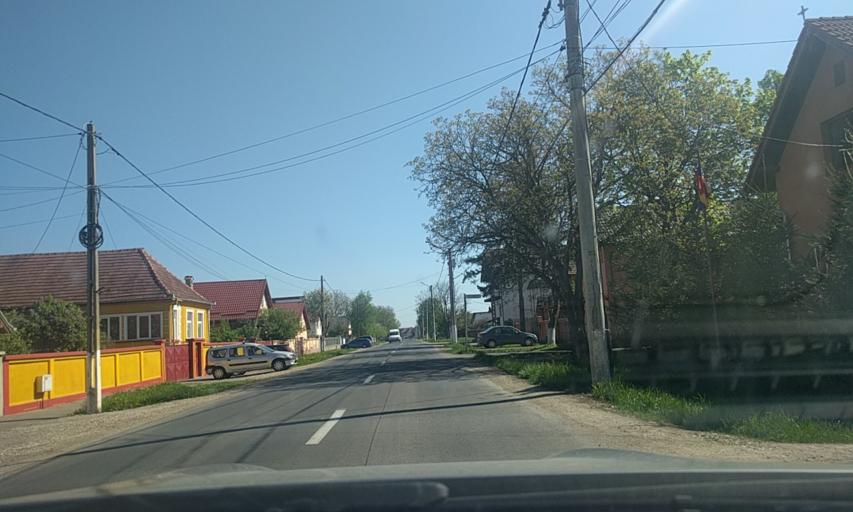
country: RO
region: Brasov
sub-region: Comuna Bod
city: Colonia Bod
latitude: 45.7024
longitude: 25.5667
